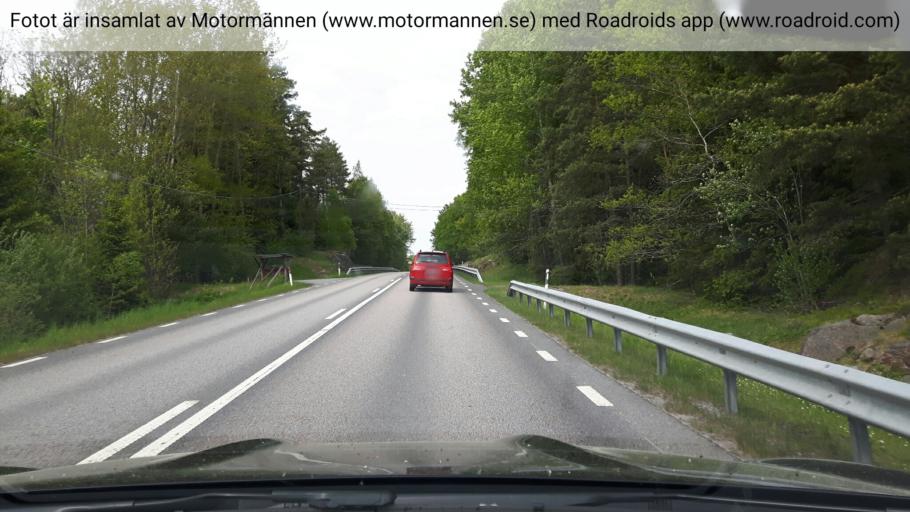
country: SE
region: Stockholm
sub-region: Norrtalje Kommun
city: Norrtalje
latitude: 59.6253
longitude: 18.6843
